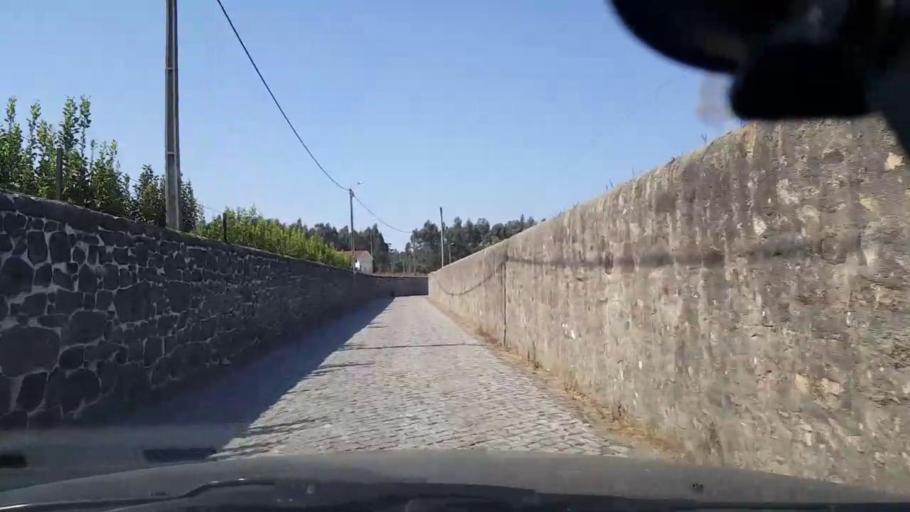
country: PT
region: Porto
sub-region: Povoa de Varzim
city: Pedroso
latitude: 41.3879
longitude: -8.7078
